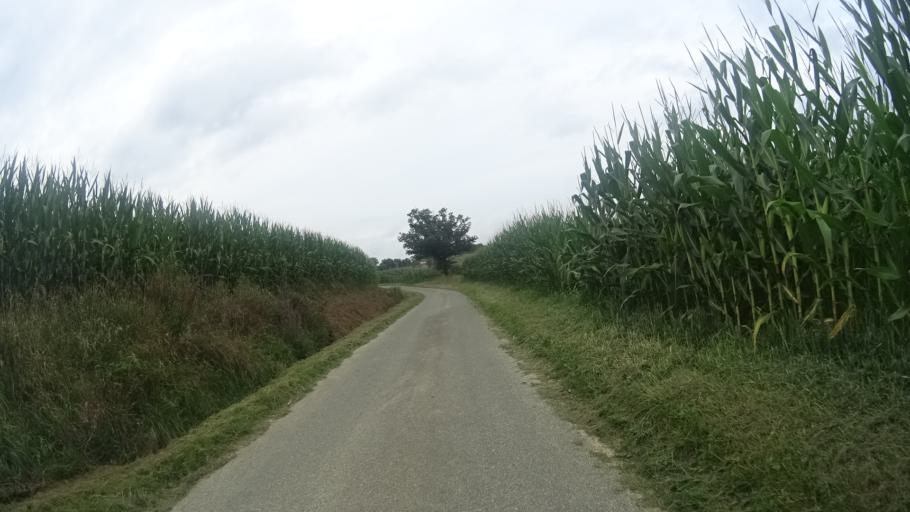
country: FR
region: Aquitaine
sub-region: Departement des Pyrenees-Atlantiques
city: Orthez
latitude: 43.4840
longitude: -0.7086
